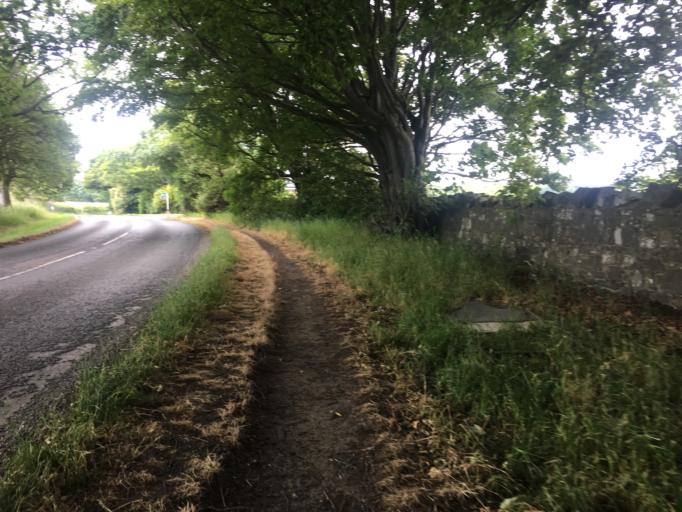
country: GB
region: England
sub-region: Northumberland
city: Bamburgh
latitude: 55.6038
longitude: -1.7666
